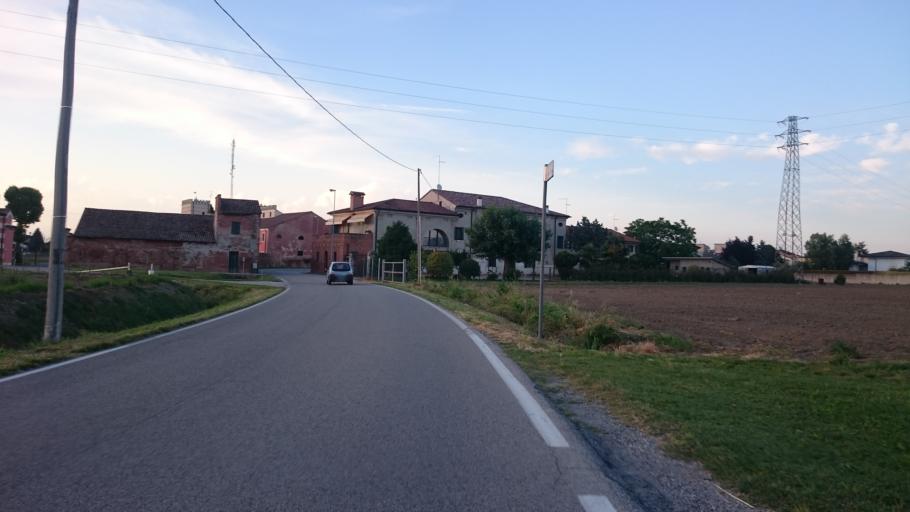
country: IT
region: Veneto
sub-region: Provincia di Verona
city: Legnago
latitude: 45.1834
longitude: 11.2733
